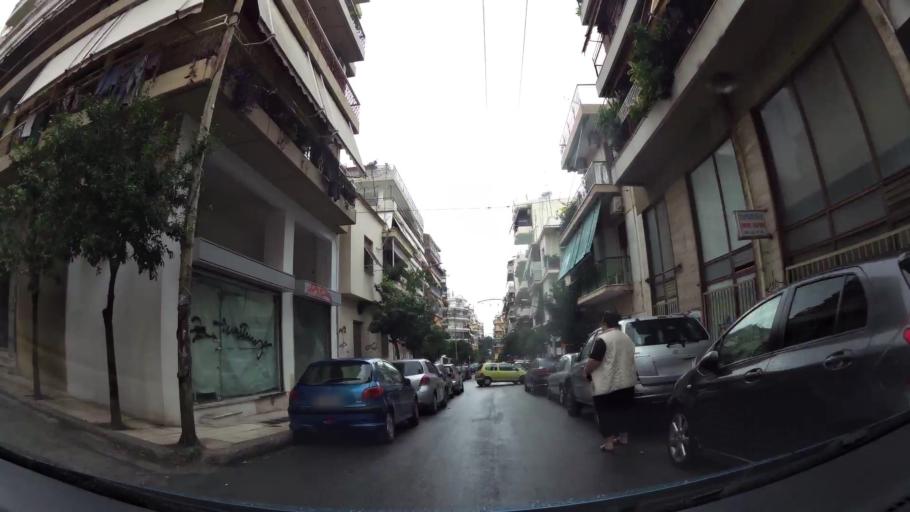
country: GR
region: Attica
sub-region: Nomarchia Athinas
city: Vyronas
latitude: 37.9580
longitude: 23.7574
